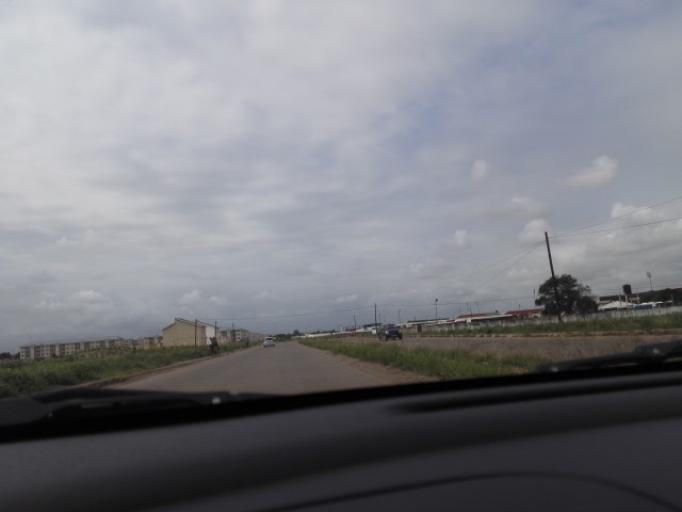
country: MZ
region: Maputo City
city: Maputo
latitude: -25.8216
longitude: 32.5829
